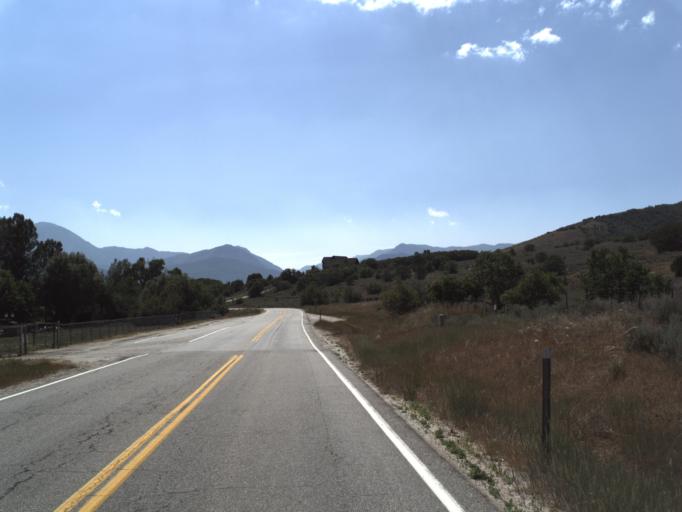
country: US
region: Utah
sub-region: Weber County
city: Wolf Creek
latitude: 41.2645
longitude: -111.6908
